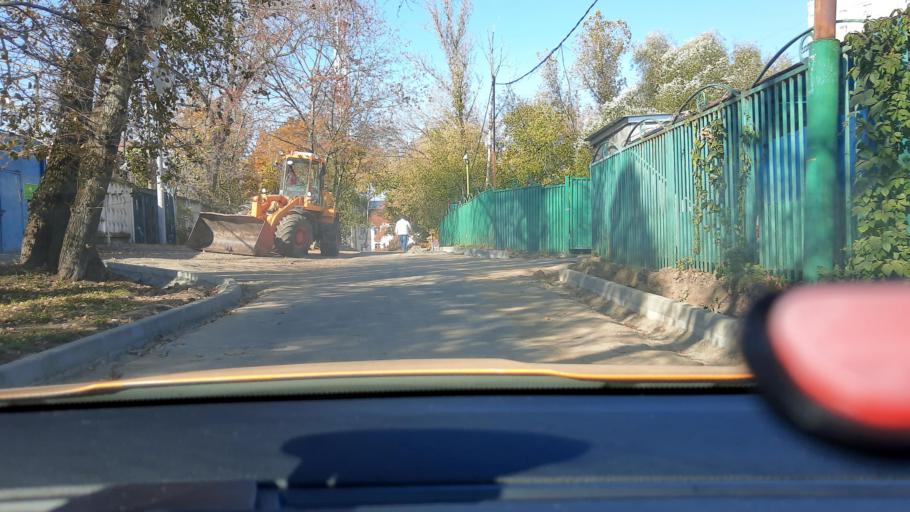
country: RU
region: Moscow
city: Strogino
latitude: 55.8377
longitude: 37.4147
